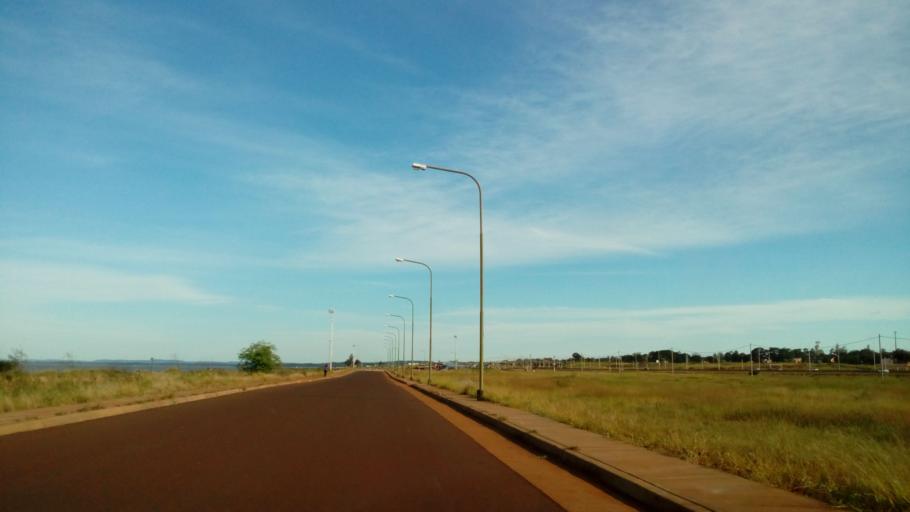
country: AR
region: Misiones
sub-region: Departamento de Capital
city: Posadas
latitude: -27.4142
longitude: -55.8836
